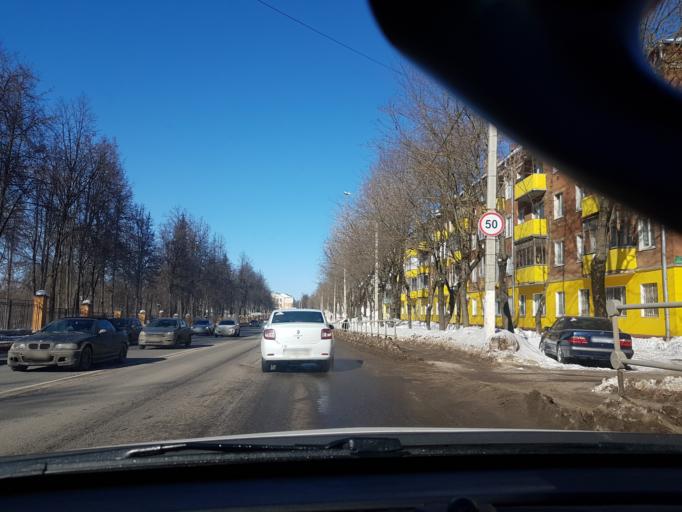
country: RU
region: Moskovskaya
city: Istra
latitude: 55.9168
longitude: 36.8584
